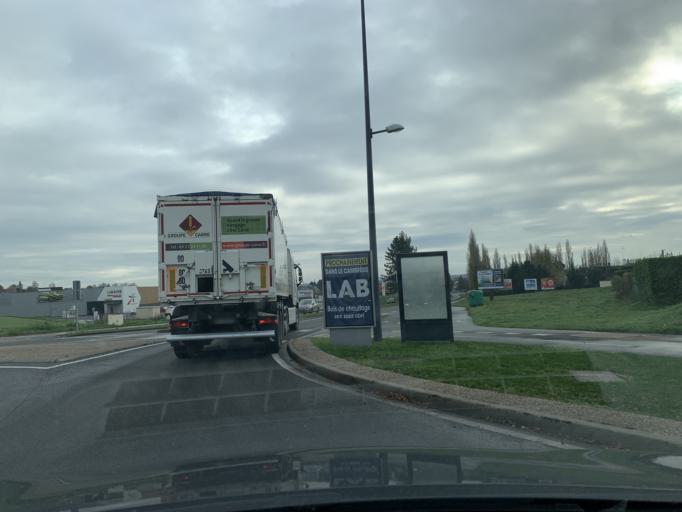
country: FR
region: Nord-Pas-de-Calais
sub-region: Departement du Nord
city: Neuville-Saint-Remy
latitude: 50.1947
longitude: 3.2094
